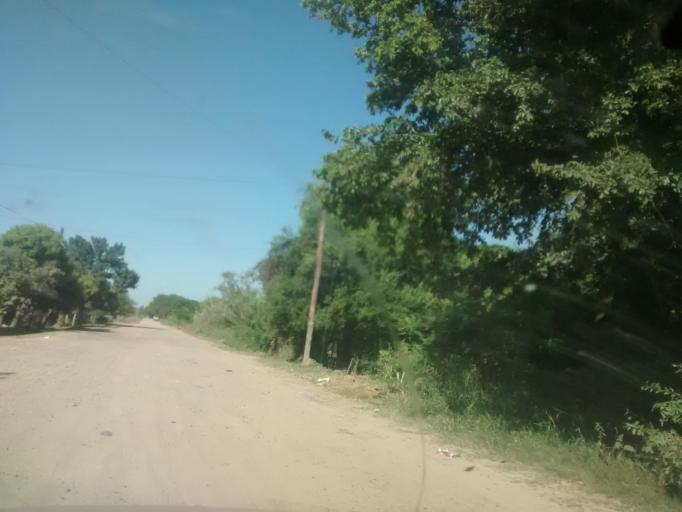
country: AR
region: Chaco
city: Resistencia
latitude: -27.4441
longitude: -58.9644
